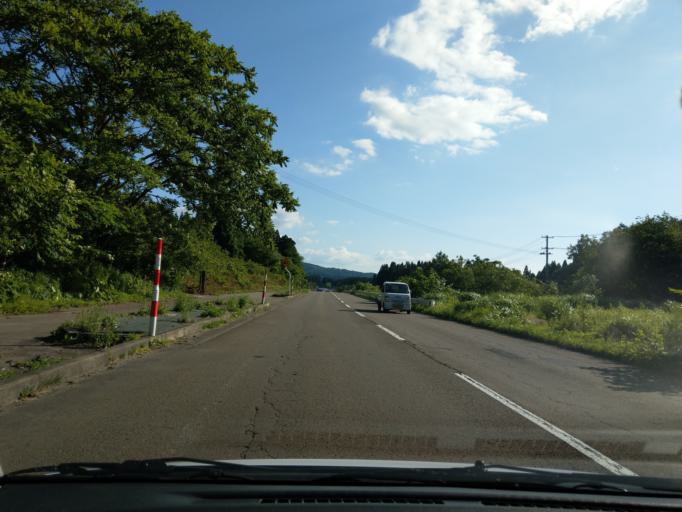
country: JP
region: Akita
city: Takanosu
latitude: 40.1400
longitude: 140.3861
